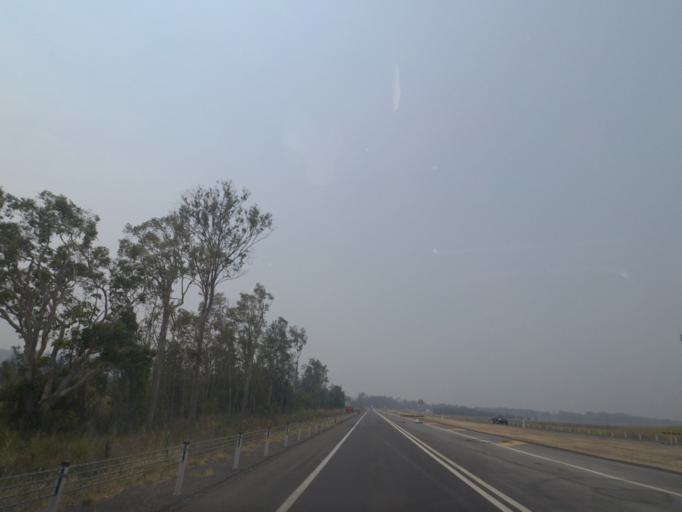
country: AU
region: New South Wales
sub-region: Ballina
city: Ballina
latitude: -28.8734
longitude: 153.4898
